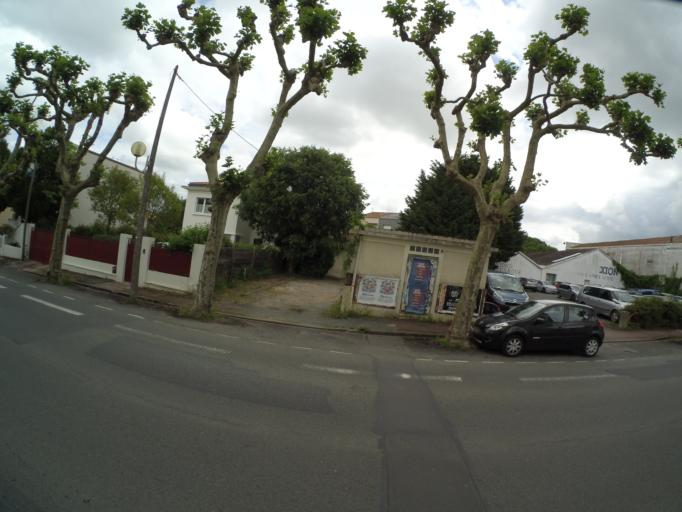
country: FR
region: Poitou-Charentes
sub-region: Departement de la Charente-Maritime
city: Rochefort
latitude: 45.9440
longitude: -0.9612
